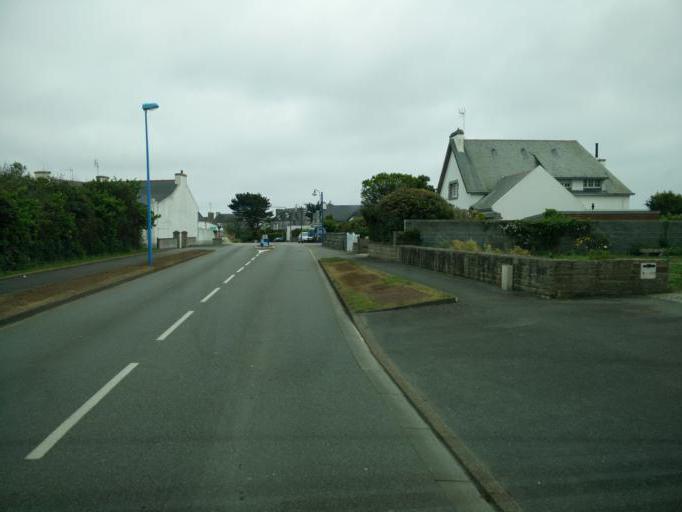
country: FR
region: Brittany
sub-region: Departement du Finistere
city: Plobannalec-Lesconil
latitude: 47.8012
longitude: -4.2212
